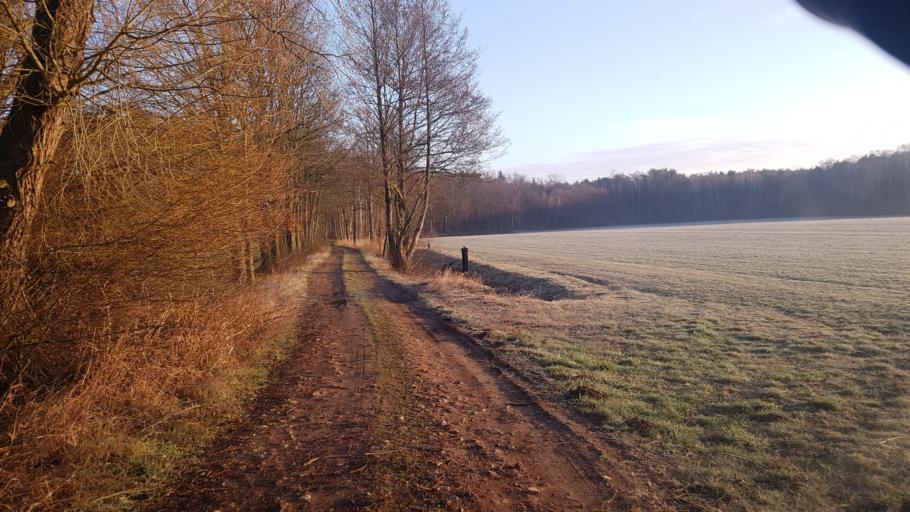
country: DE
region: Brandenburg
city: Finsterwalde
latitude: 51.6705
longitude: 13.7490
